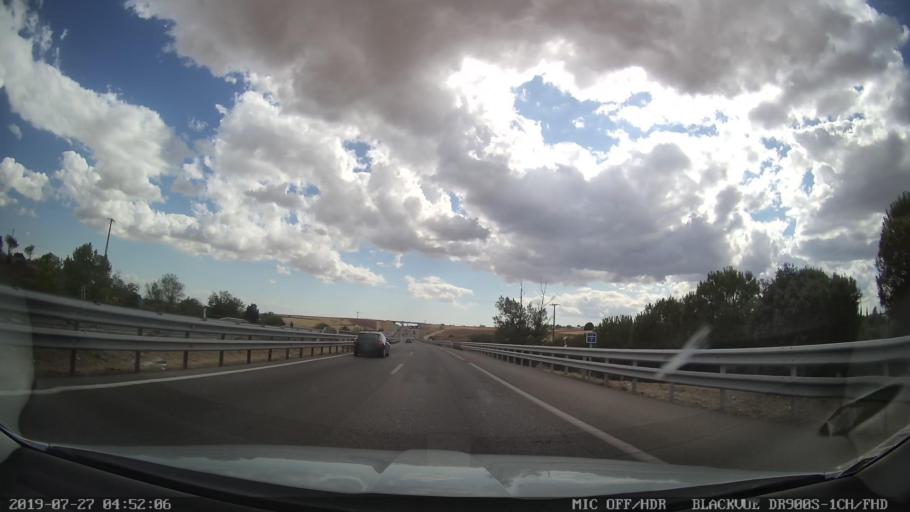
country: ES
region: Madrid
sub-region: Provincia de Madrid
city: Navalcarnero
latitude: 40.2894
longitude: -3.9936
